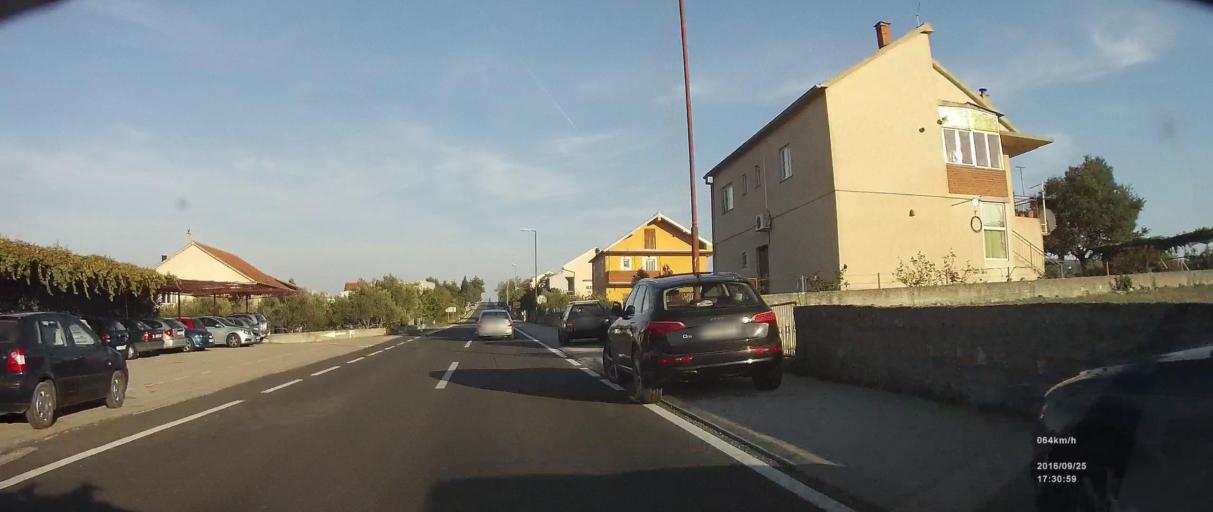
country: HR
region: Sibensko-Kniniska
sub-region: Grad Sibenik
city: Brodarica
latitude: 43.6791
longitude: 15.9842
